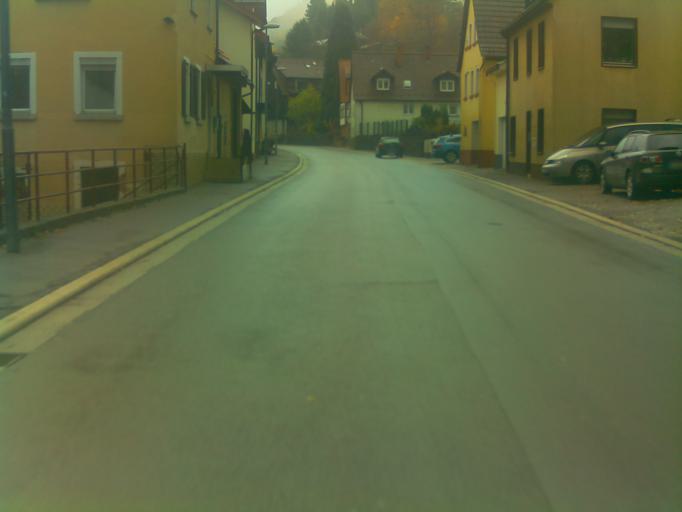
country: DE
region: Baden-Wuerttemberg
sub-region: Karlsruhe Region
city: Schonau
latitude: 49.4588
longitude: 8.8071
